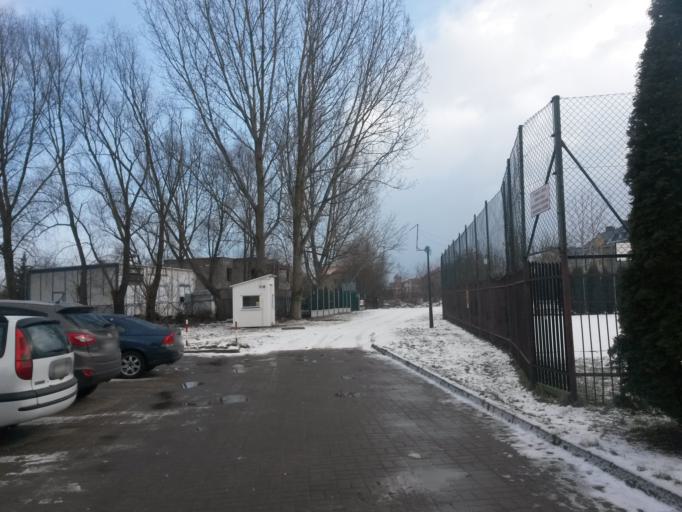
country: PL
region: Masovian Voivodeship
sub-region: Powiat wolominski
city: Zabki
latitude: 52.2901
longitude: 21.0832
